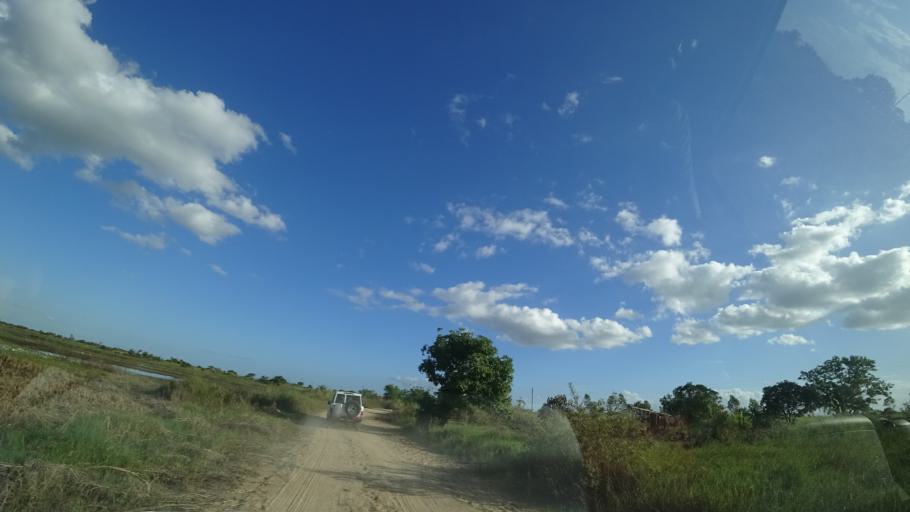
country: MZ
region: Sofala
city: Dondo
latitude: -19.4273
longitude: 34.5613
